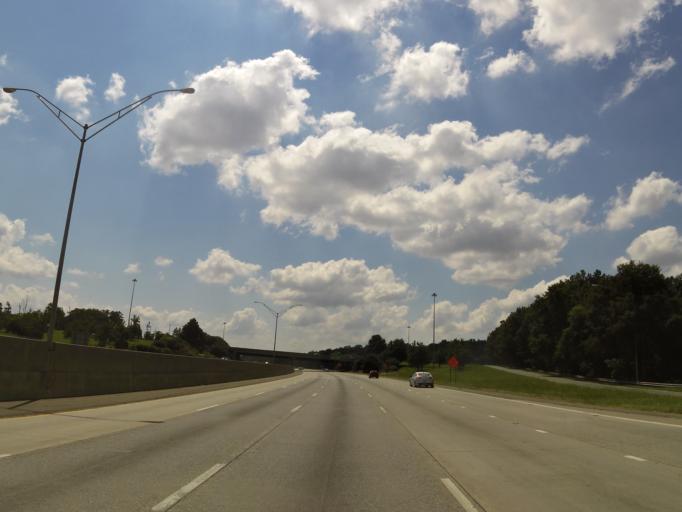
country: US
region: North Carolina
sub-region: Cabarrus County
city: Harrisburg
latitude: 35.3144
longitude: -80.7571
